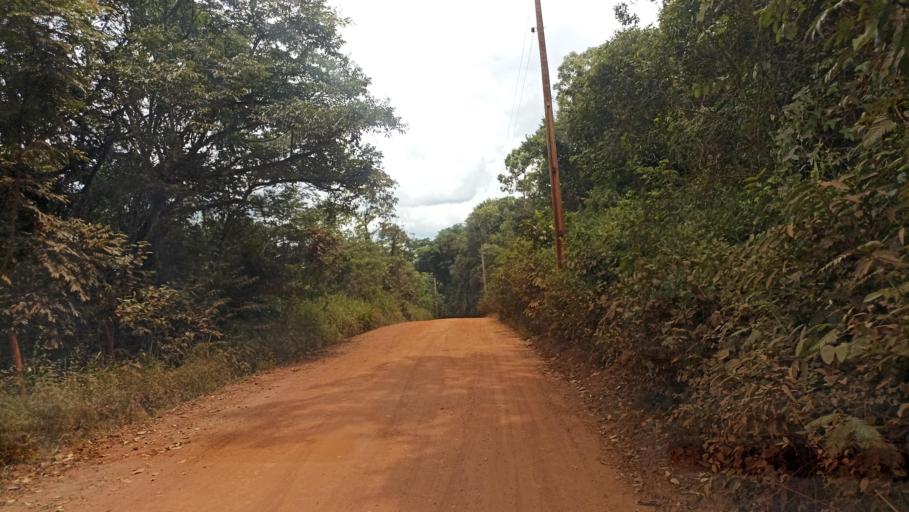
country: BR
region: Minas Gerais
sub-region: Itabirito
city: Itabirito
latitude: -20.3384
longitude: -43.7562
